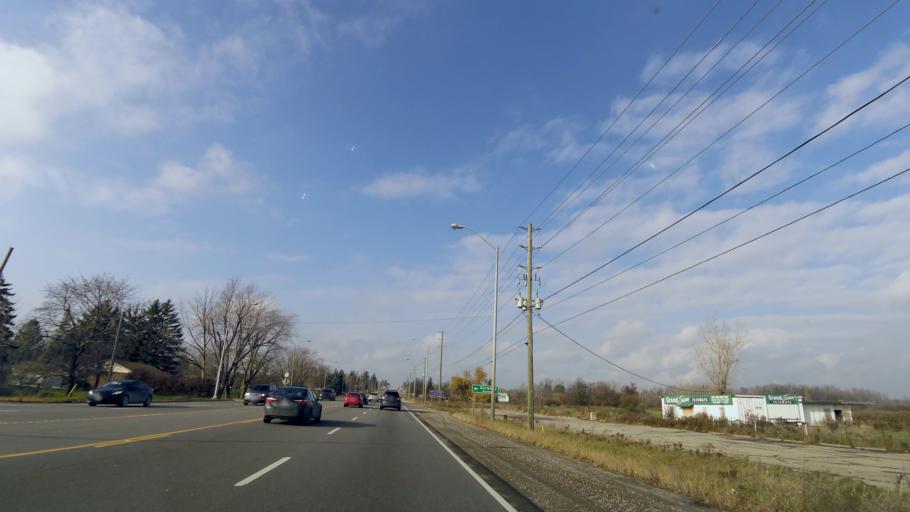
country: CA
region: Ontario
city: Hamilton
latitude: 43.3161
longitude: -79.9227
